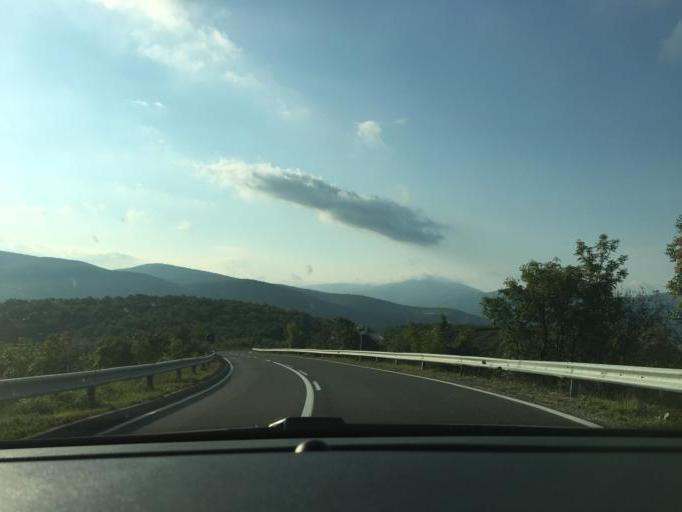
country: MK
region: Valandovo
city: Valandovo
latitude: 41.3331
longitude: 22.5926
